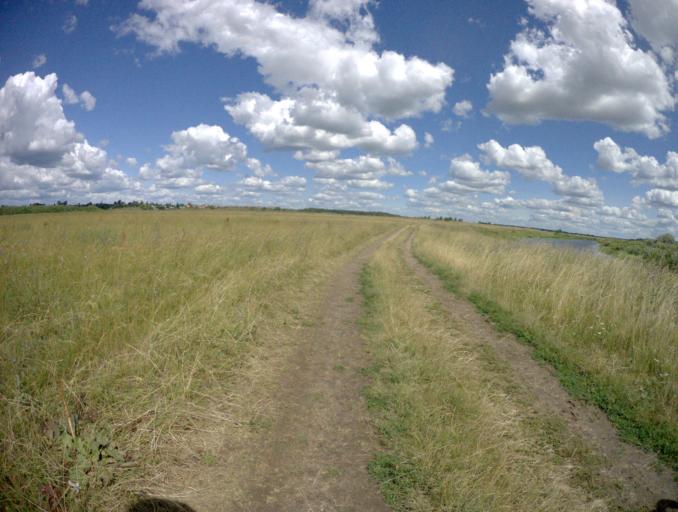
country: RU
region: Vladimir
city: Orgtrud
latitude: 56.3003
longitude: 40.6174
